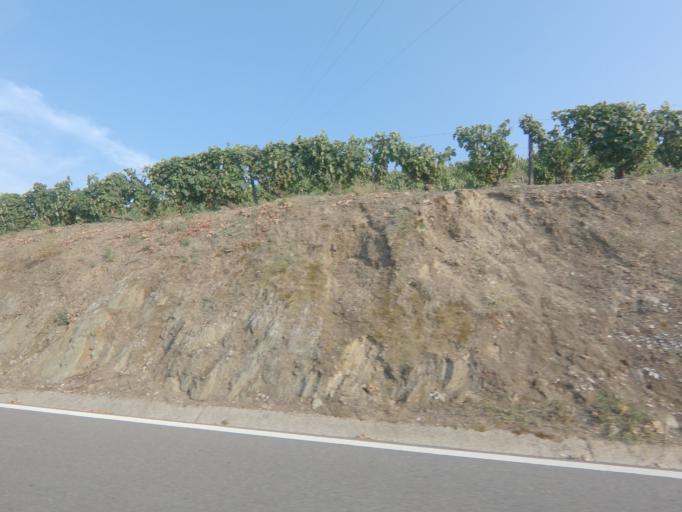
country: PT
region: Viseu
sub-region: Armamar
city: Armamar
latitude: 41.1535
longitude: -7.6346
